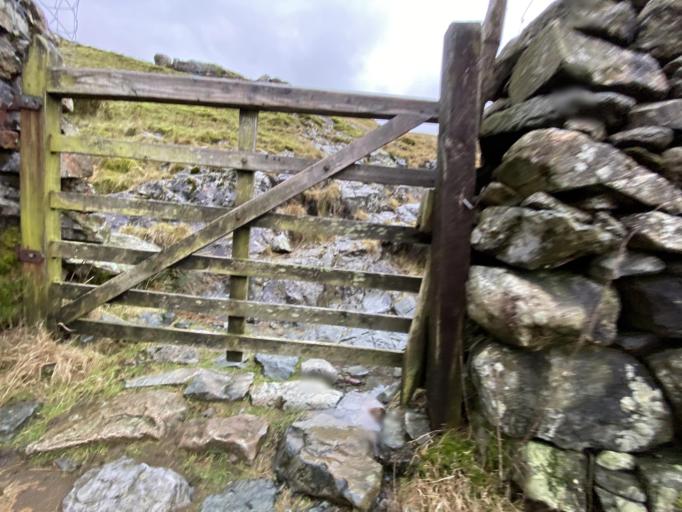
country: GB
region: England
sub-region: Cumbria
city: Keswick
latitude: 54.4873
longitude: -3.1874
